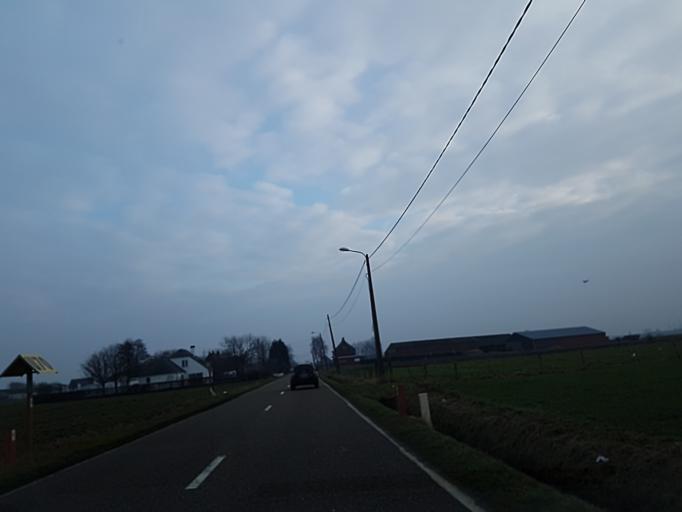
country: BE
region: Flanders
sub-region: Provincie Antwerpen
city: Stabroek
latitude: 51.3208
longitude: 4.3784
